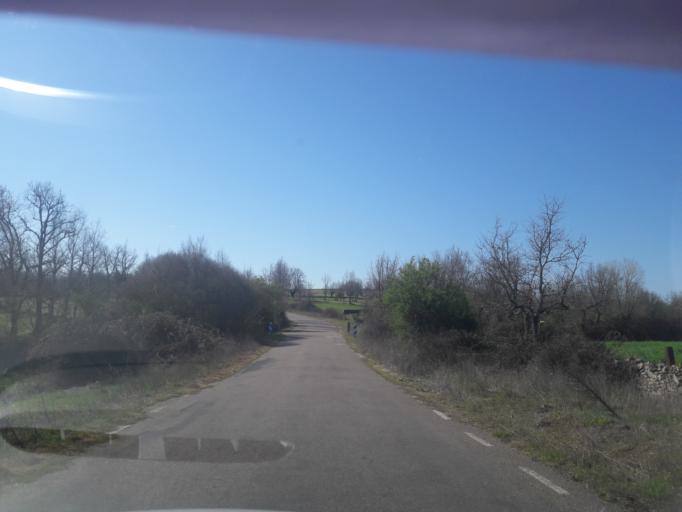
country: ES
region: Castille and Leon
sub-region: Provincia de Salamanca
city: Valsalabroso
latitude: 41.1453
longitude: -6.4862
